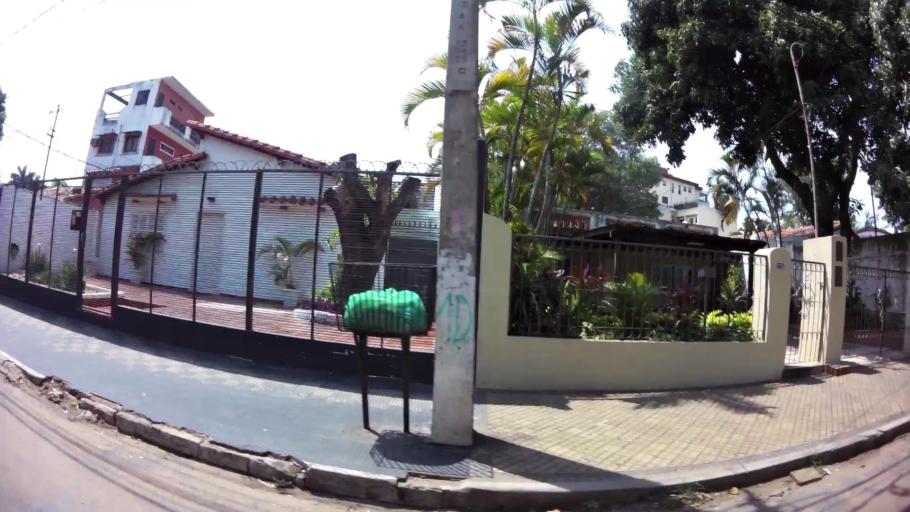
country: PY
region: Asuncion
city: Asuncion
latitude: -25.2818
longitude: -57.5901
